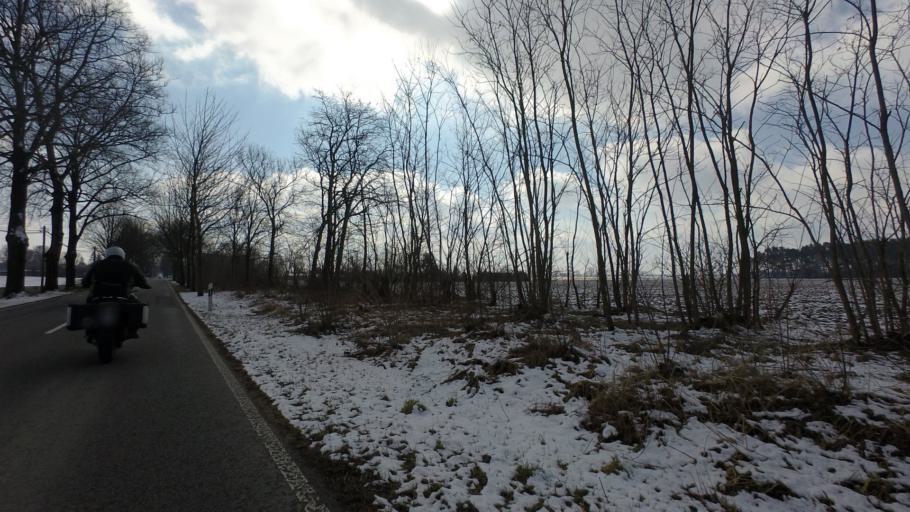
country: DE
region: Brandenburg
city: Rudnitz
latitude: 52.7008
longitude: 13.6514
